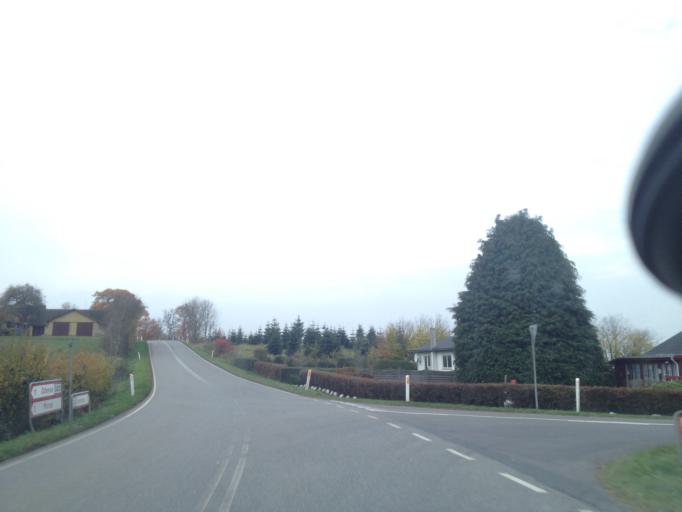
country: DK
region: South Denmark
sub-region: Assens Kommune
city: Vissenbjerg
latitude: 55.4483
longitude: 10.1554
